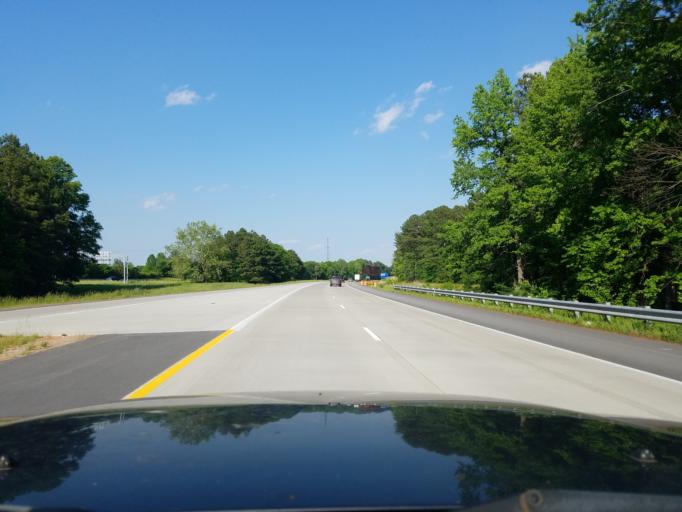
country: US
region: North Carolina
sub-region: Vance County
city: Henderson
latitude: 36.3376
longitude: -78.4308
